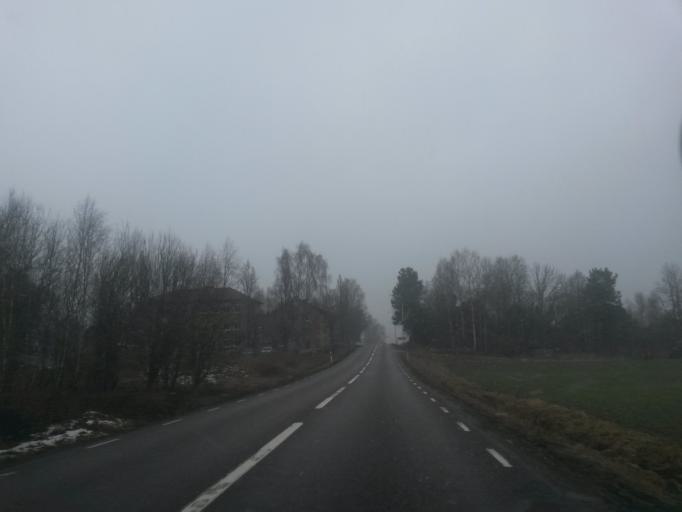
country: SE
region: Vaestra Goetaland
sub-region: Vanersborgs Kommun
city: Vargon
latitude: 58.2406
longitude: 12.4233
